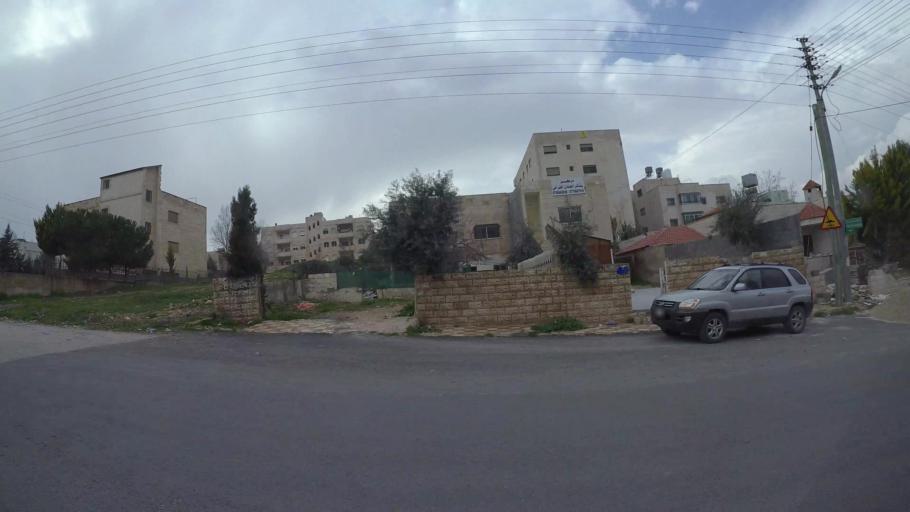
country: JO
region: Amman
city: Umm as Summaq
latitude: 31.8824
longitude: 35.8597
